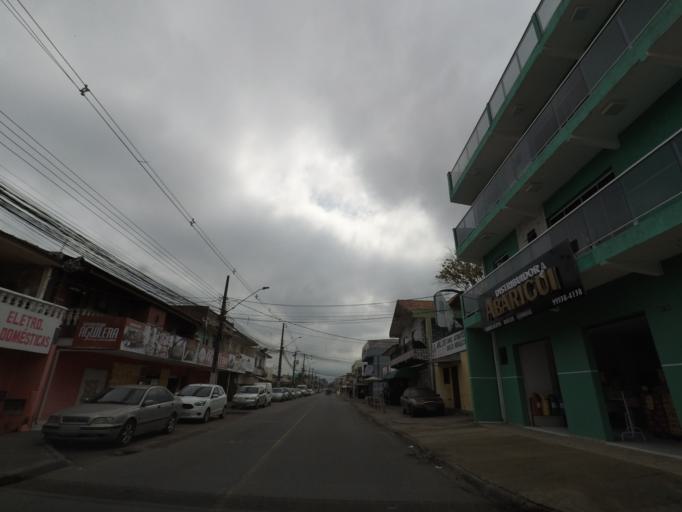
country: BR
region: Parana
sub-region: Curitiba
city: Curitiba
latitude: -25.5007
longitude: -49.3379
